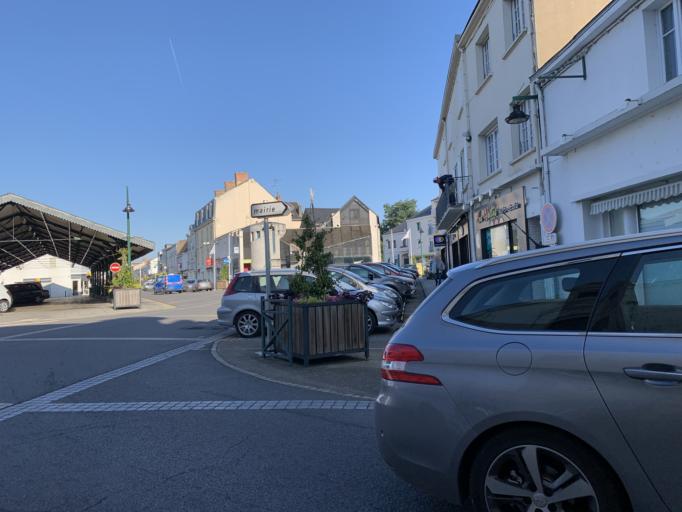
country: FR
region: Pays de la Loire
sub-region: Departement de la Loire-Atlantique
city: Machecoul
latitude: 46.9921
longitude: -1.8185
